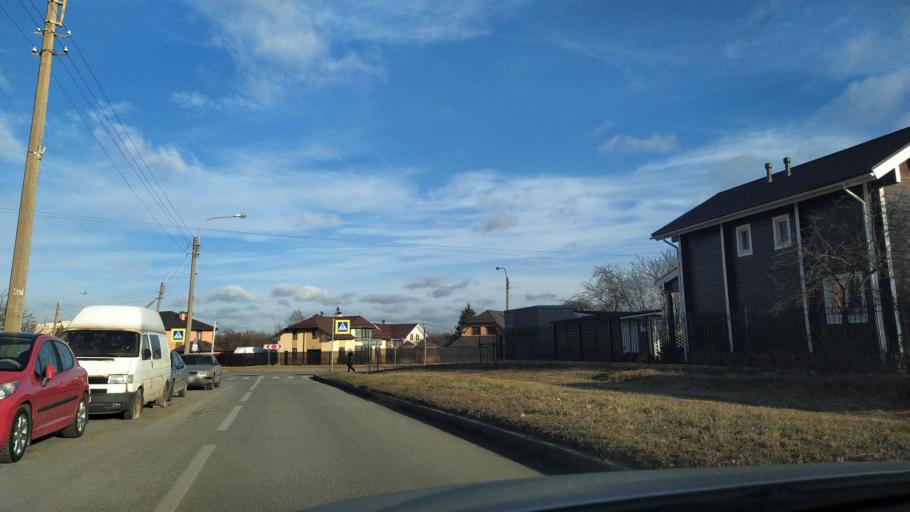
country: RU
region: St.-Petersburg
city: Pushkin
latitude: 59.7343
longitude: 30.4058
